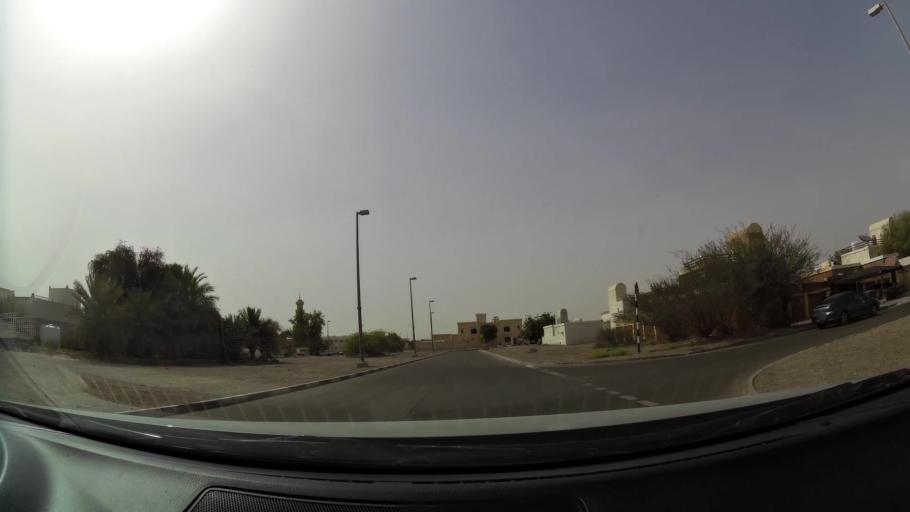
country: AE
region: Abu Dhabi
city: Al Ain
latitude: 24.1914
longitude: 55.6385
